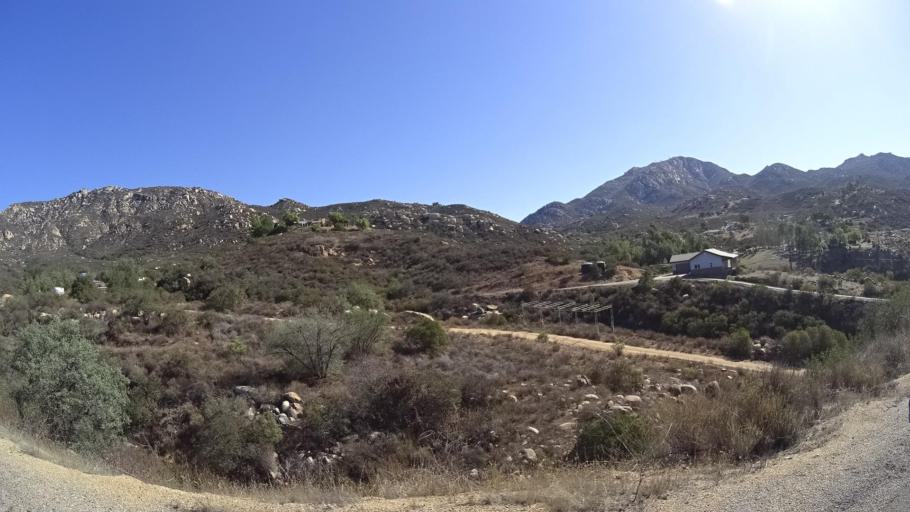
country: US
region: California
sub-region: San Diego County
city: Jamul
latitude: 32.7094
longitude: -116.7986
